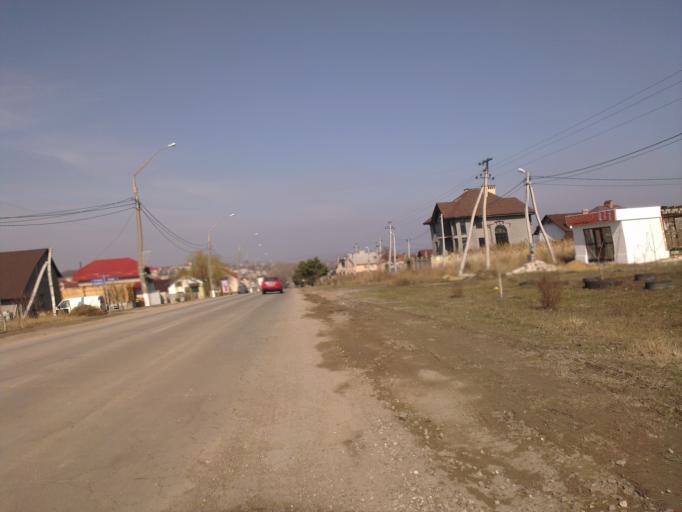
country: MD
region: Chisinau
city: Cricova
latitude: 47.1200
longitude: 28.8672
